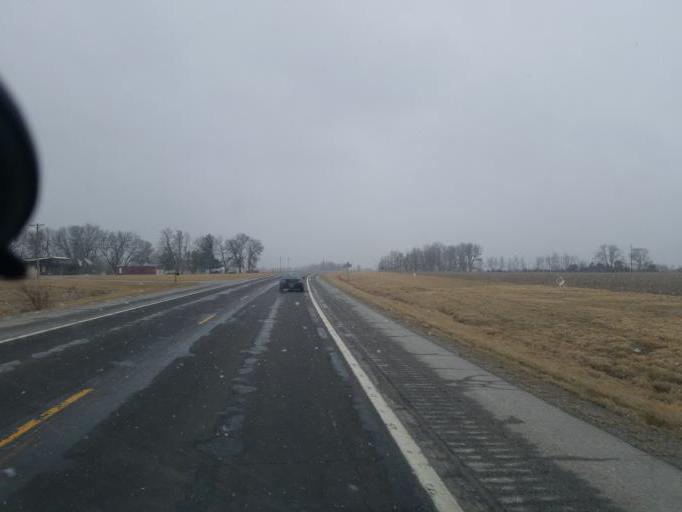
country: US
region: Missouri
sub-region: Schuyler County
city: Lancaster
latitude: 40.4058
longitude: -92.5595
